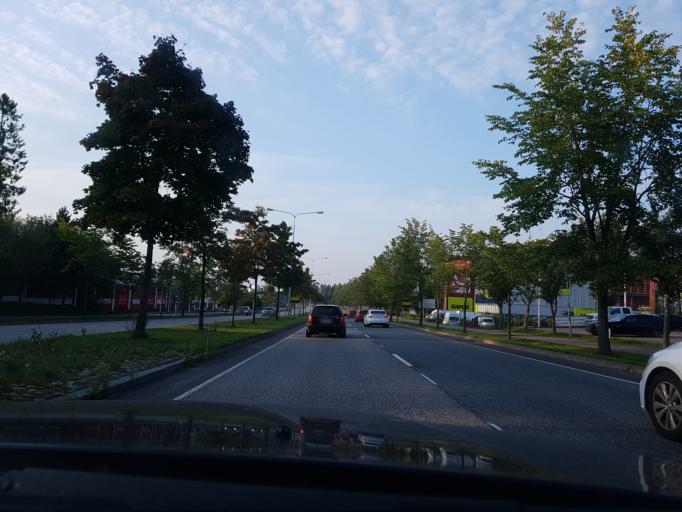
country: FI
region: Uusimaa
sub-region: Helsinki
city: Tuusula
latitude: 60.3846
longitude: 25.0256
